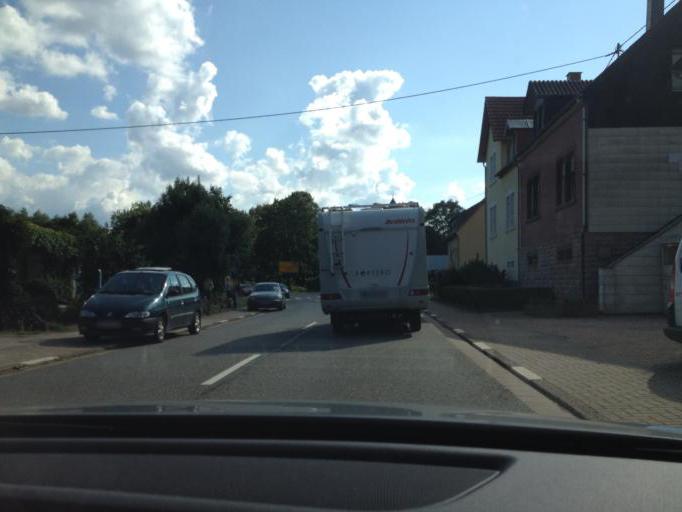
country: DE
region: Saarland
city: Mainzweiler
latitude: 49.3996
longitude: 7.0828
